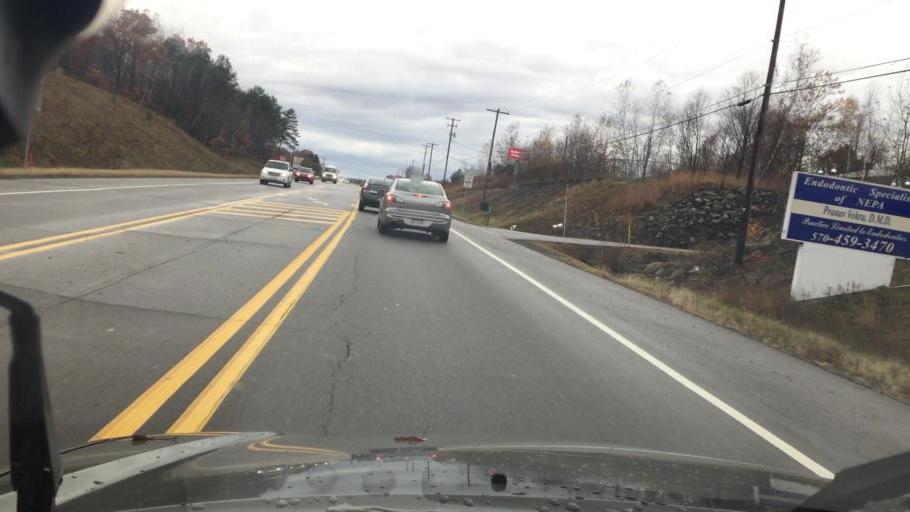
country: US
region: Pennsylvania
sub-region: Luzerne County
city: Harleigh
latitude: 40.9923
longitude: -75.9978
